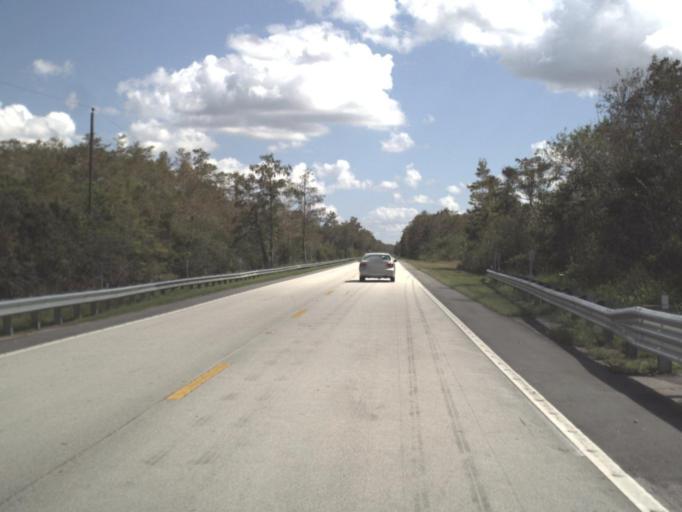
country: US
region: Florida
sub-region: Miami-Dade County
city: Kendall West
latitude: 25.8128
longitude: -80.8818
